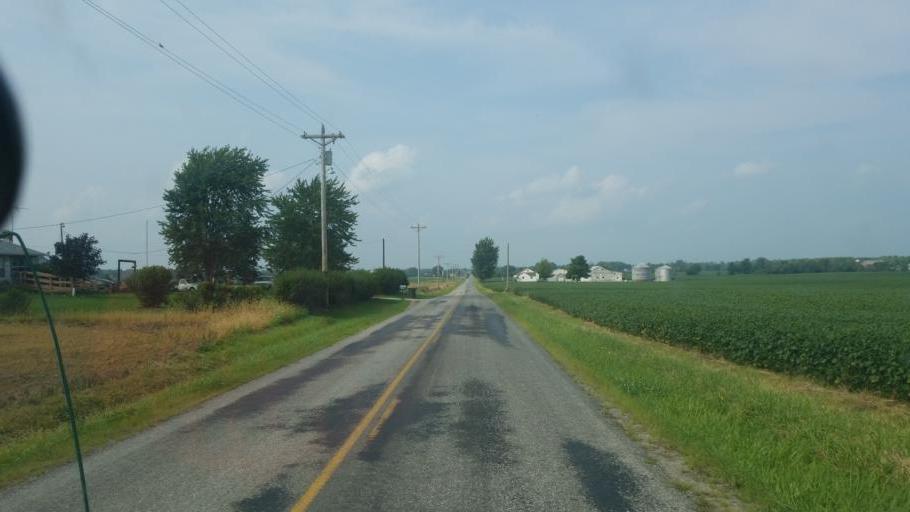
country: US
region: Ohio
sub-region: Lorain County
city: Wellington
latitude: 41.1069
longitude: -82.1611
